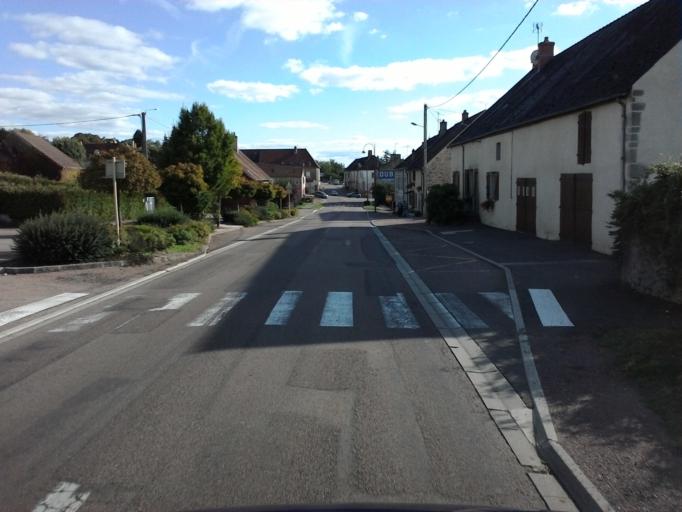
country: FR
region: Bourgogne
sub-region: Departement de la Cote-d'Or
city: Semur-en-Auxois
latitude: 47.3914
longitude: 4.3075
